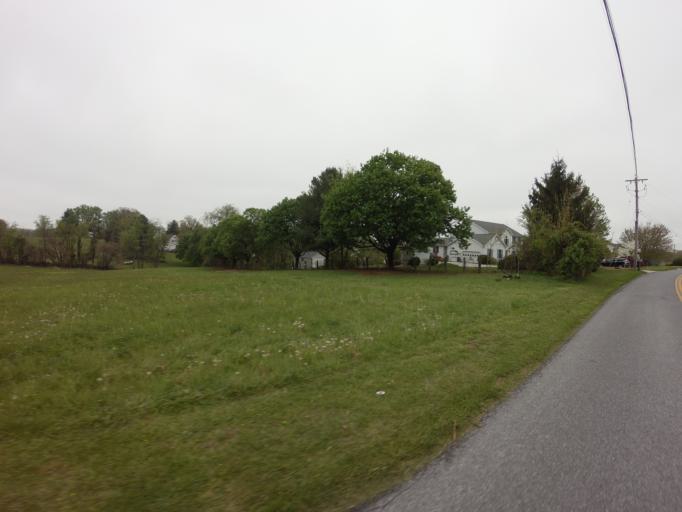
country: US
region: Maryland
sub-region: Baltimore County
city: Hunt Valley
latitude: 39.5739
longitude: -76.7229
